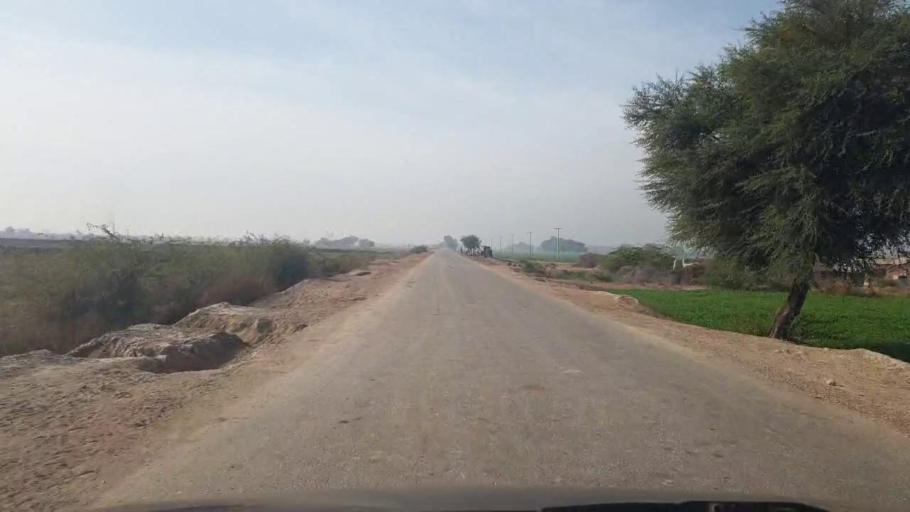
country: PK
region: Sindh
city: Umarkot
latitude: 25.3604
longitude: 69.7020
